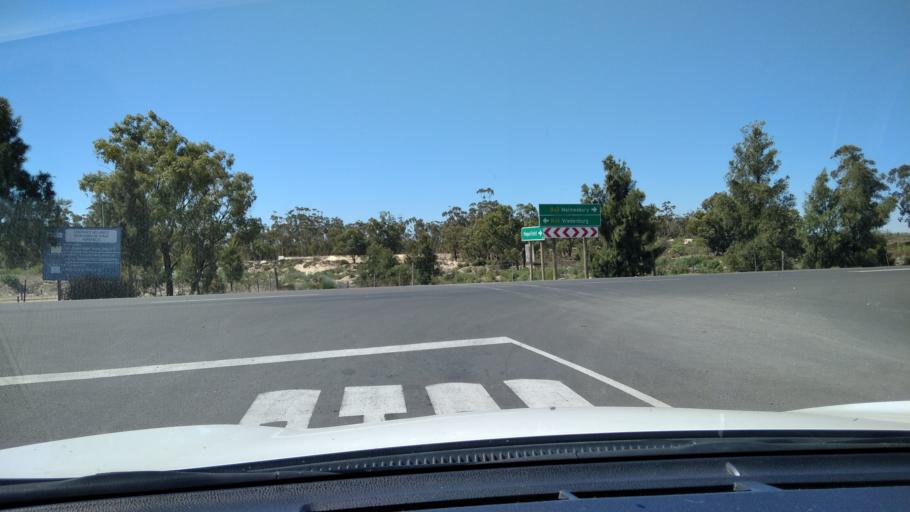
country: ZA
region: Western Cape
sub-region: West Coast District Municipality
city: Moorreesburg
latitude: -33.0633
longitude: 18.3585
